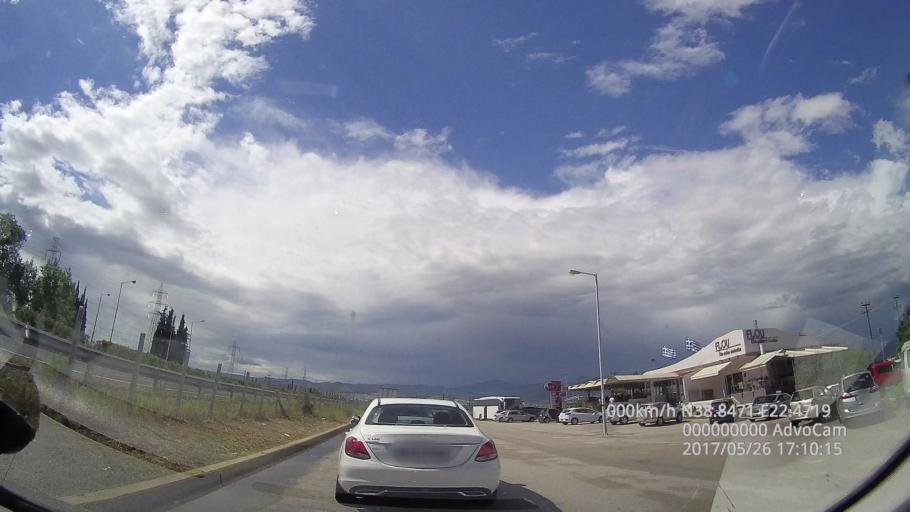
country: GR
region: Central Greece
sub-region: Nomos Fthiotidos
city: Pelasgia
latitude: 38.9678
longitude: 22.8895
